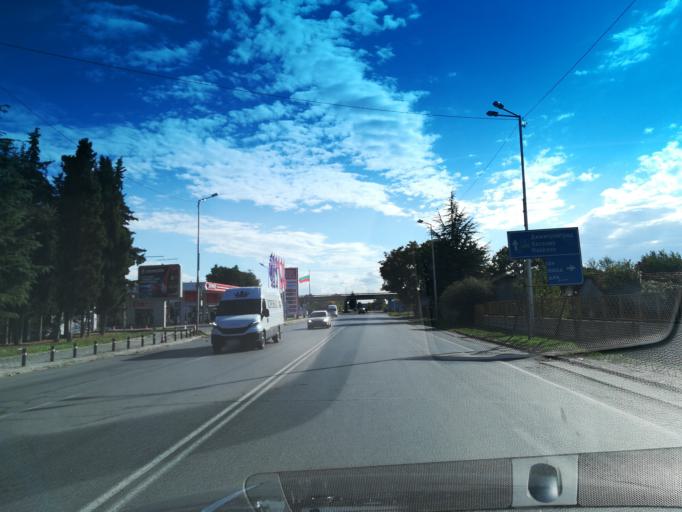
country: BG
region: Stara Zagora
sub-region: Obshtina Stara Zagora
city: Stara Zagora
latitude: 42.3955
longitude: 25.6453
